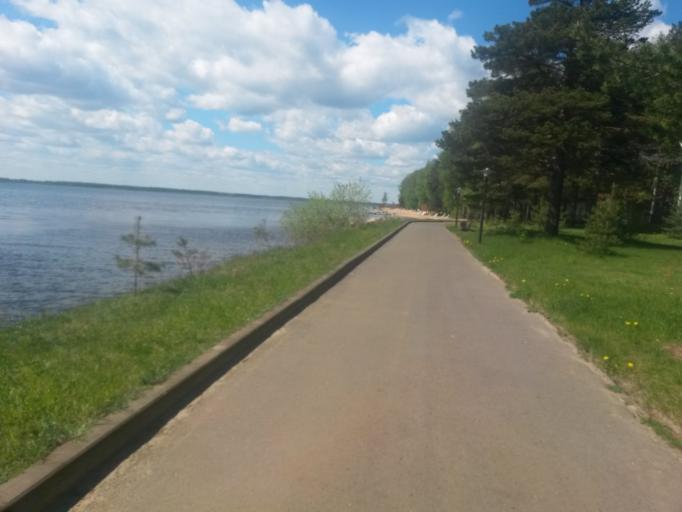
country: RU
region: Jaroslavl
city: Borok
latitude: 58.0626
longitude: 38.3454
